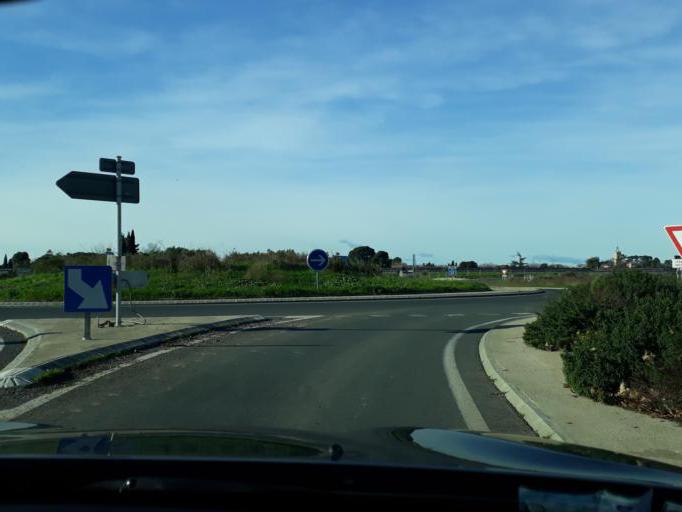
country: FR
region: Languedoc-Roussillon
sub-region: Departement de l'Herault
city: Pezenas
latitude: 43.4525
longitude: 3.4323
